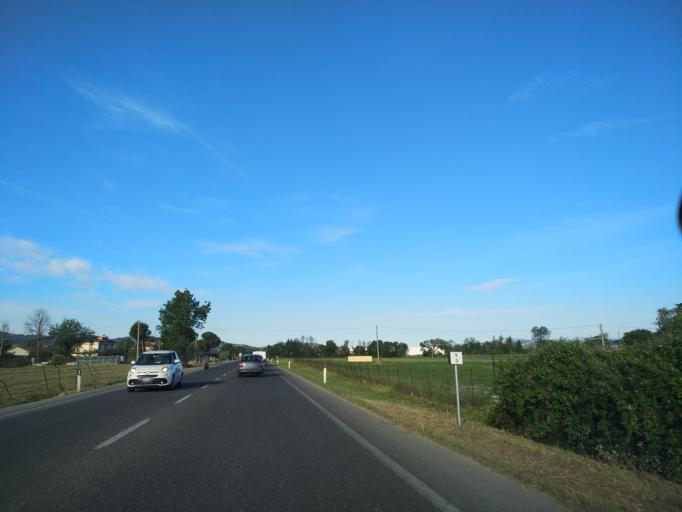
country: IT
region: The Marches
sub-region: Provincia di Pesaro e Urbino
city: Villa Ceccolini
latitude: 43.8767
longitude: 12.8460
